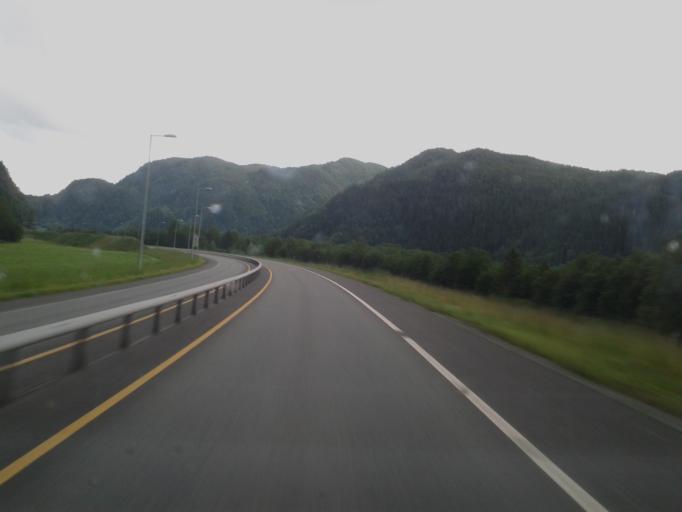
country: NO
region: Sor-Trondelag
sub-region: Midtre Gauldal
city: Storen
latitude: 63.0865
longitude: 10.2502
